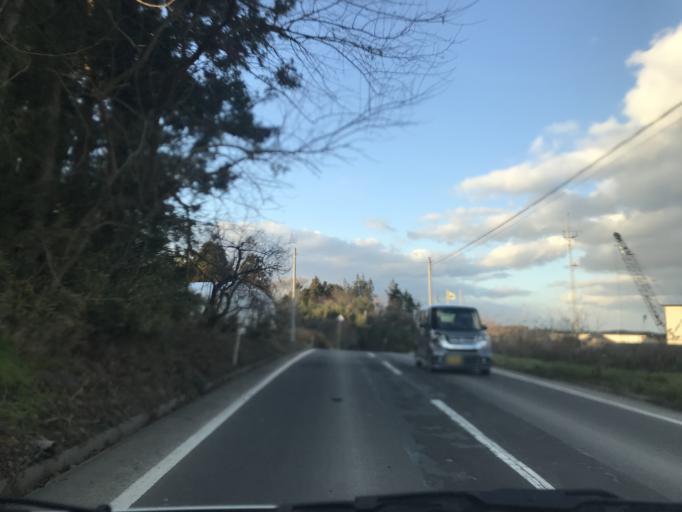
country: JP
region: Miyagi
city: Kogota
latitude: 38.6351
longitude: 141.0695
